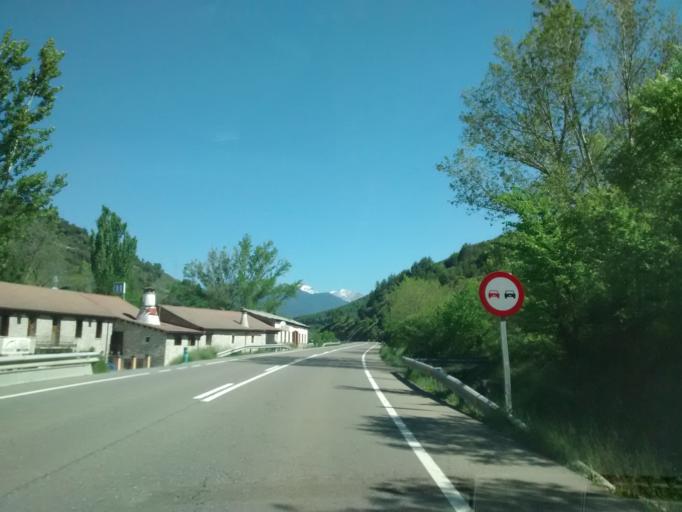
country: ES
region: Aragon
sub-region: Provincia de Huesca
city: Jaca
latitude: 42.5981
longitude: -0.5438
